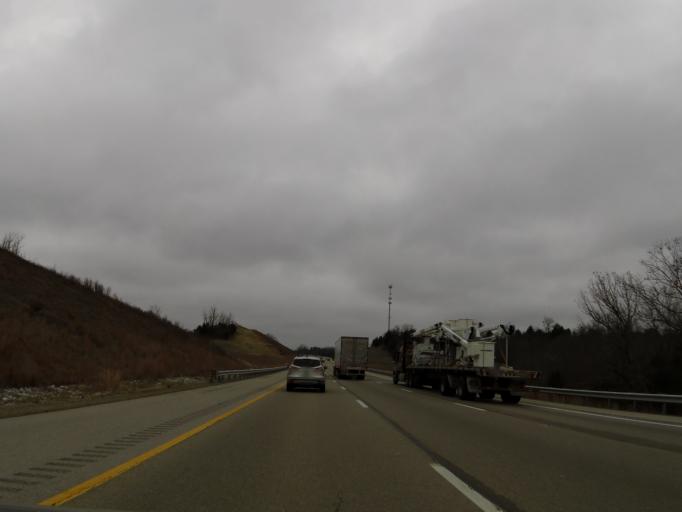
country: US
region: Kentucky
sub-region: Grant County
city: Williamstown
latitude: 38.5646
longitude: -84.5947
